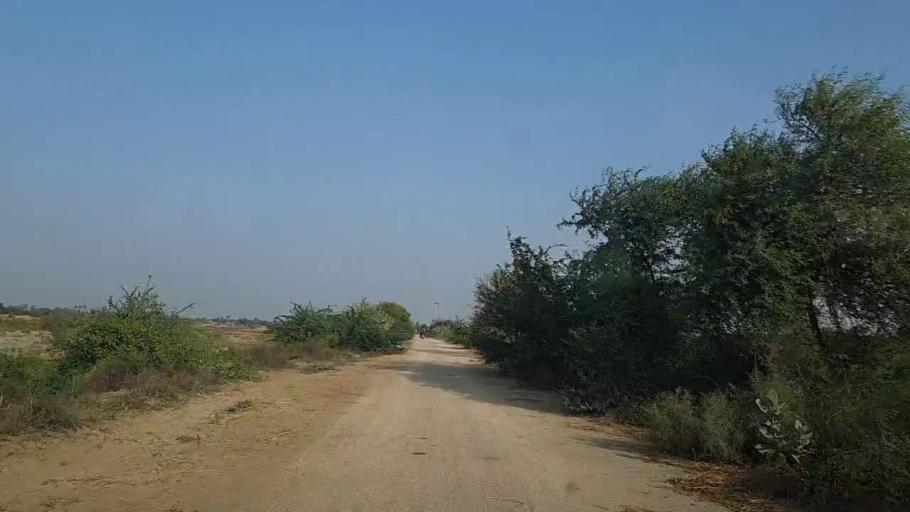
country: PK
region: Sindh
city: Mirpur Sakro
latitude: 24.5746
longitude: 67.6823
